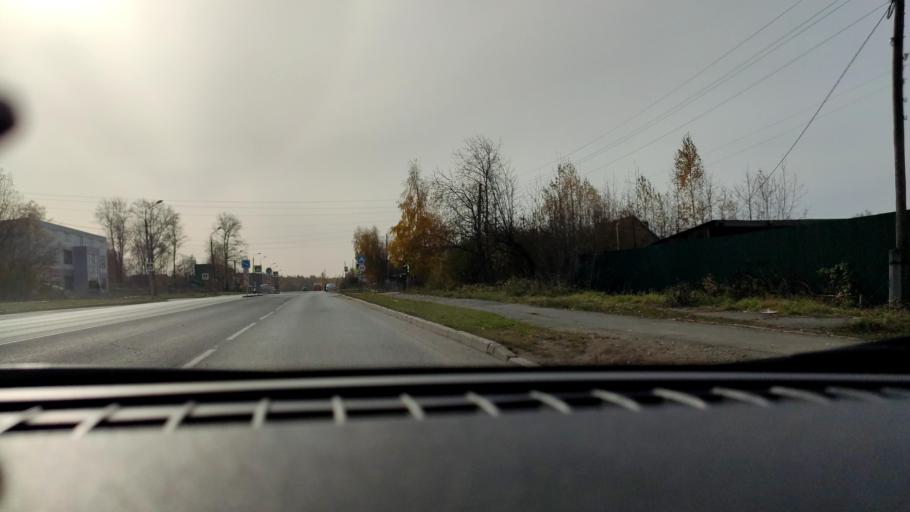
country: RU
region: Perm
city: Polazna
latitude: 58.1180
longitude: 56.4021
